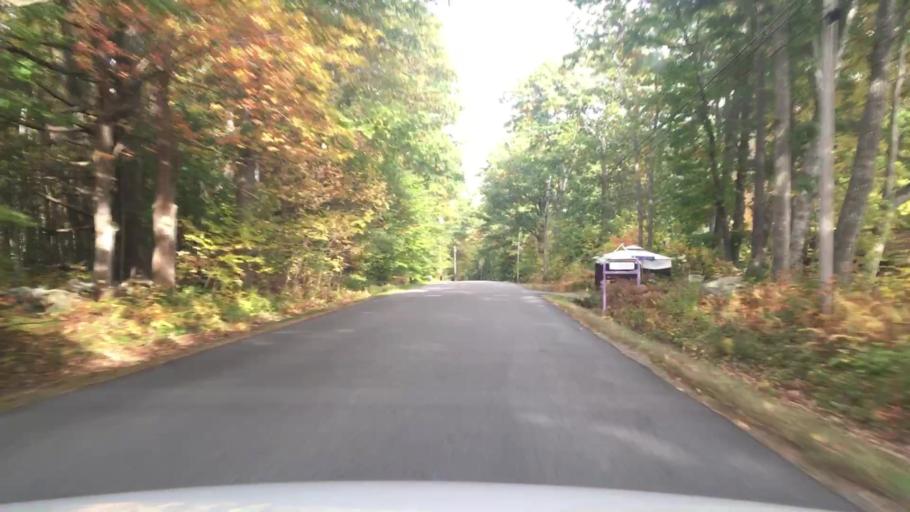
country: US
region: Maine
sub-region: Knox County
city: Camden
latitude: 44.2221
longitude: -69.1022
